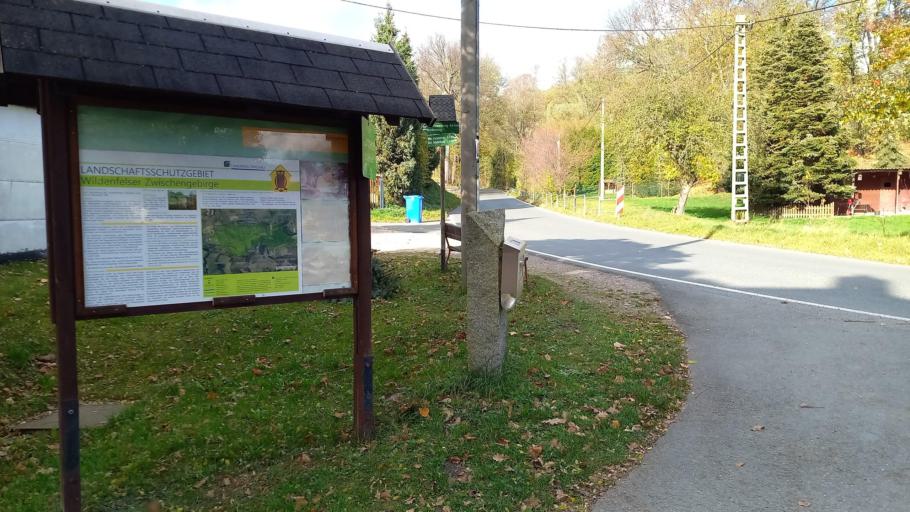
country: DE
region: Saxony
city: Wildenfels
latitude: 50.6467
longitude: 12.6085
